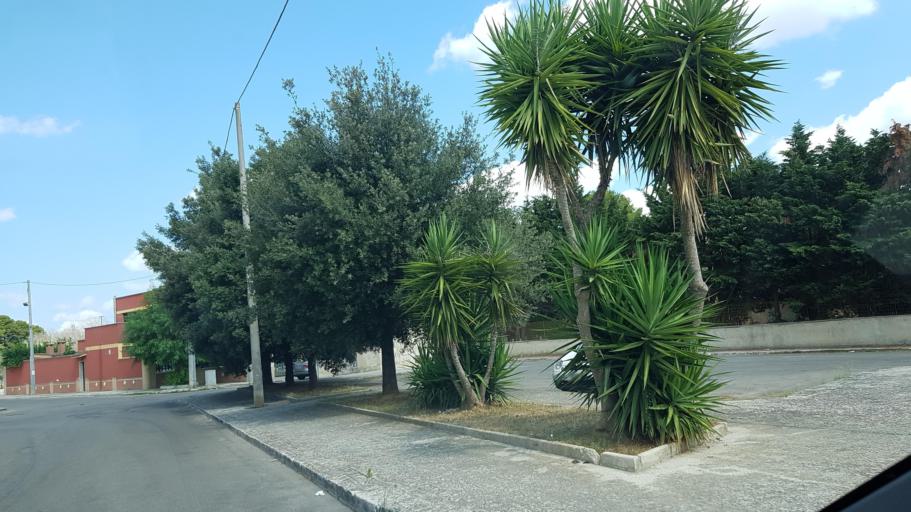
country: IT
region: Apulia
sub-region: Provincia di Lecce
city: Trepuzzi
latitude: 40.4094
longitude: 18.0639
